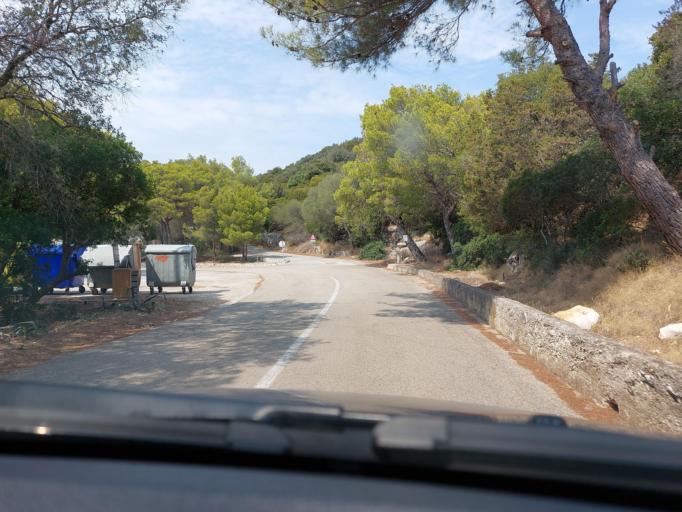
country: HR
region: Dubrovacko-Neretvanska
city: Smokvica
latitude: 42.7643
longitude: 16.8236
